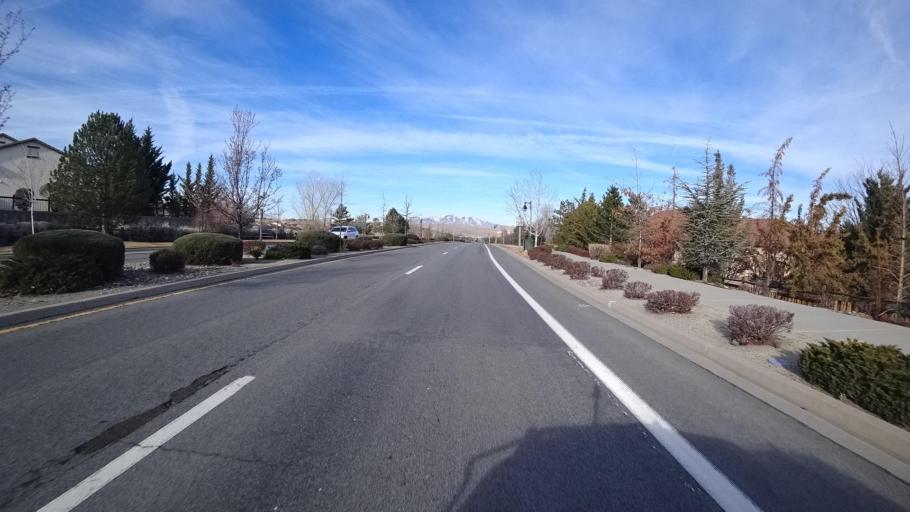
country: US
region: Nevada
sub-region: Washoe County
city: Spanish Springs
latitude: 39.6072
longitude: -119.6805
